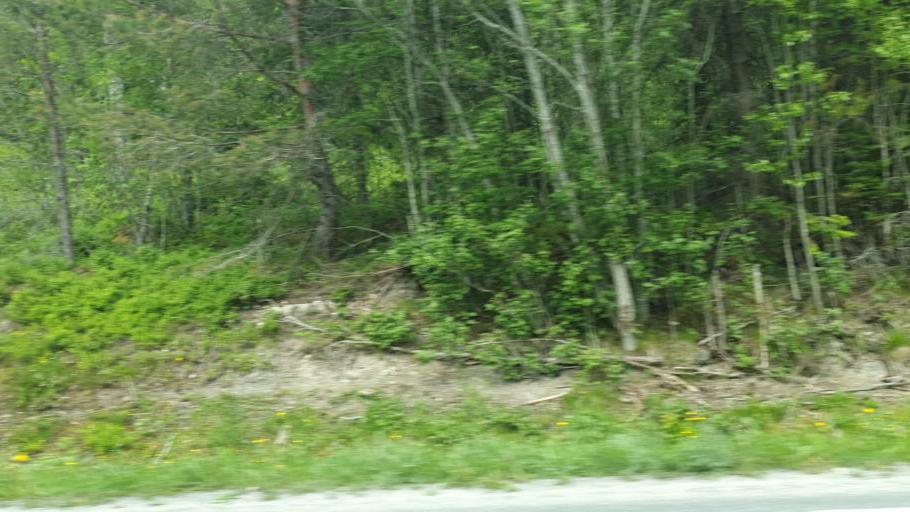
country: NO
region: Sor-Trondelag
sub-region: Trondheim
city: Trondheim
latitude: 63.5586
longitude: 10.3128
